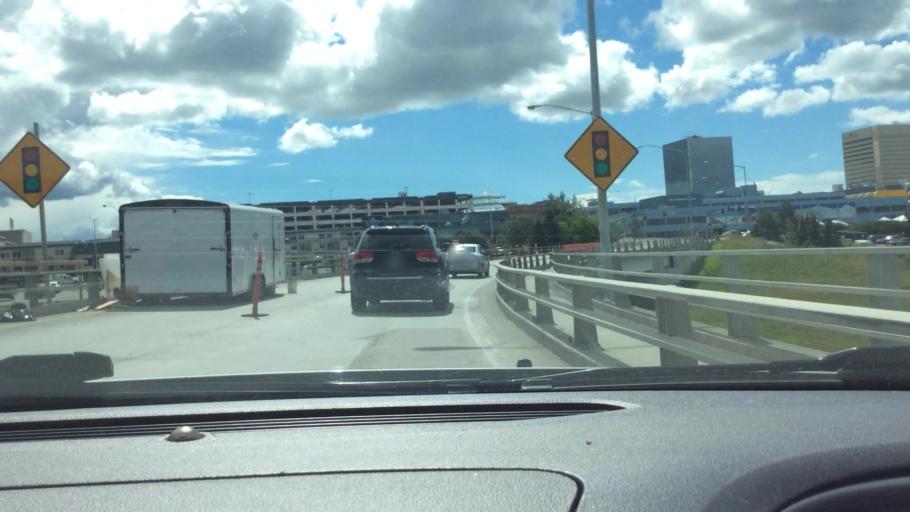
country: US
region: Alaska
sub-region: Anchorage Municipality
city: Anchorage
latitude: 61.2211
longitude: -149.8855
